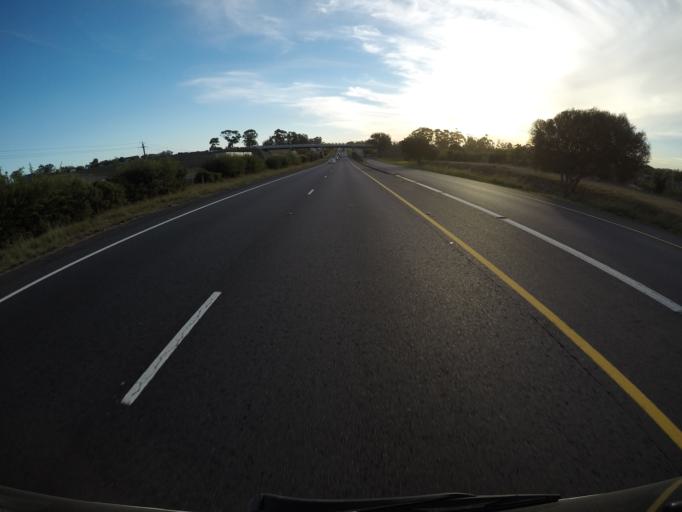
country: ZA
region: Western Cape
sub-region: City of Cape Town
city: Kraaifontein
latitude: -33.8191
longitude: 18.7940
